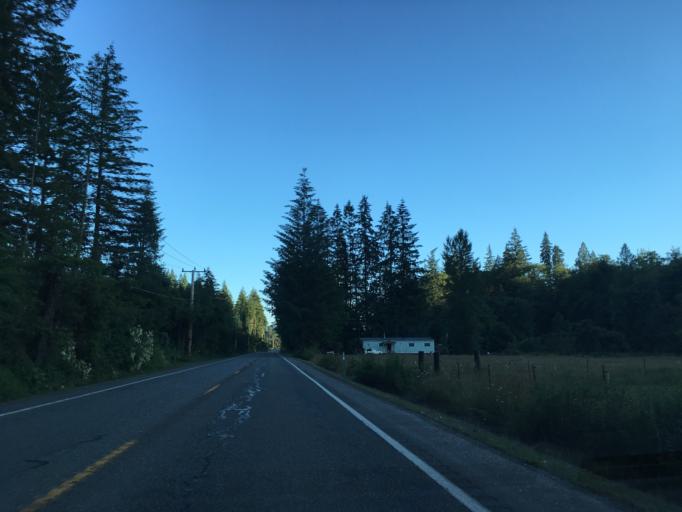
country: US
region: Washington
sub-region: Whatcom County
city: Peaceful Valley
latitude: 48.9231
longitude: -122.1433
